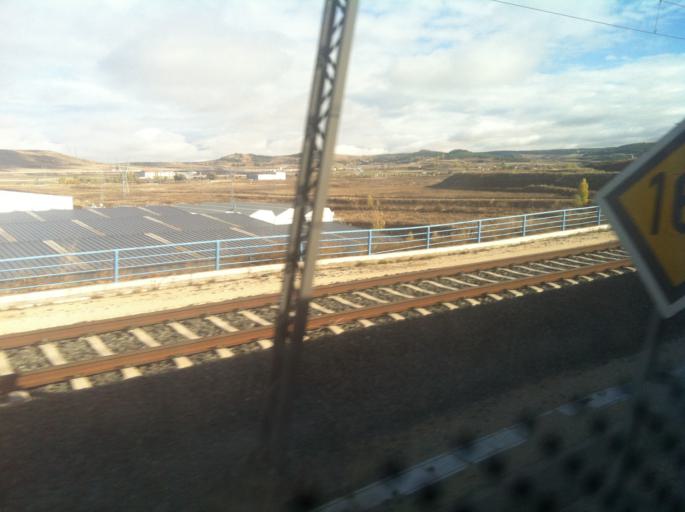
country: ES
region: Castille and Leon
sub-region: Provincia de Burgos
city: Burgos
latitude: 42.3684
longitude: -3.7107
